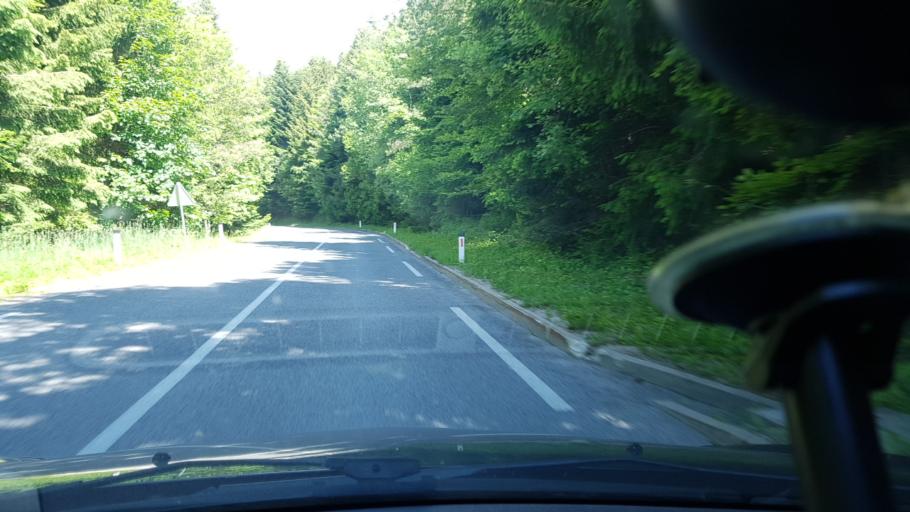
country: SI
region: Zrece
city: Zrece
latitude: 46.4227
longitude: 15.3727
